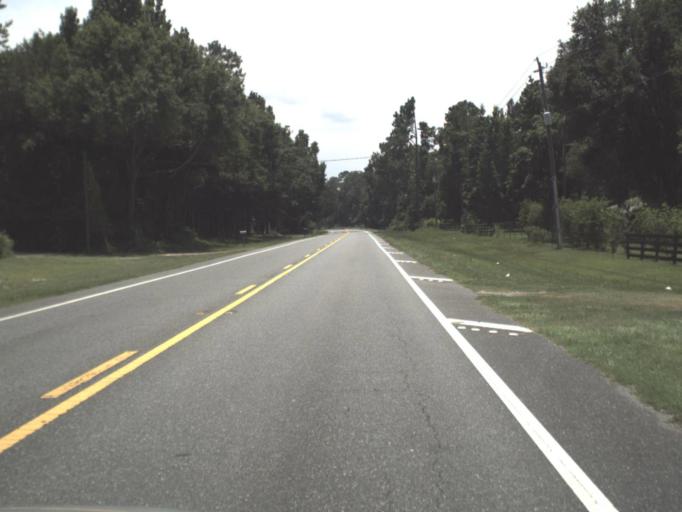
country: US
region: Florida
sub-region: Bradford County
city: Starke
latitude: 30.0281
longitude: -82.1577
